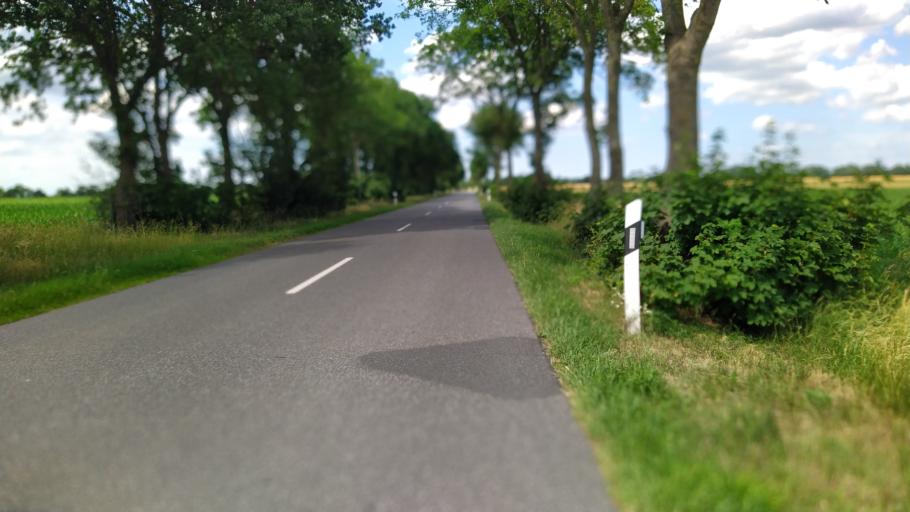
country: DE
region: Lower Saxony
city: Hollnseth
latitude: 53.5781
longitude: 9.1117
